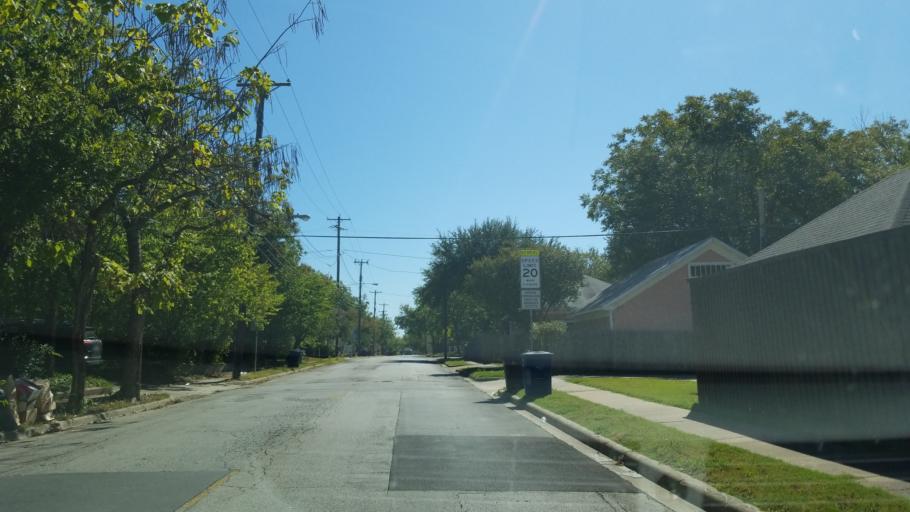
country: US
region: Texas
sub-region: Dallas County
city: Highland Park
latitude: 32.8048
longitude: -96.7606
